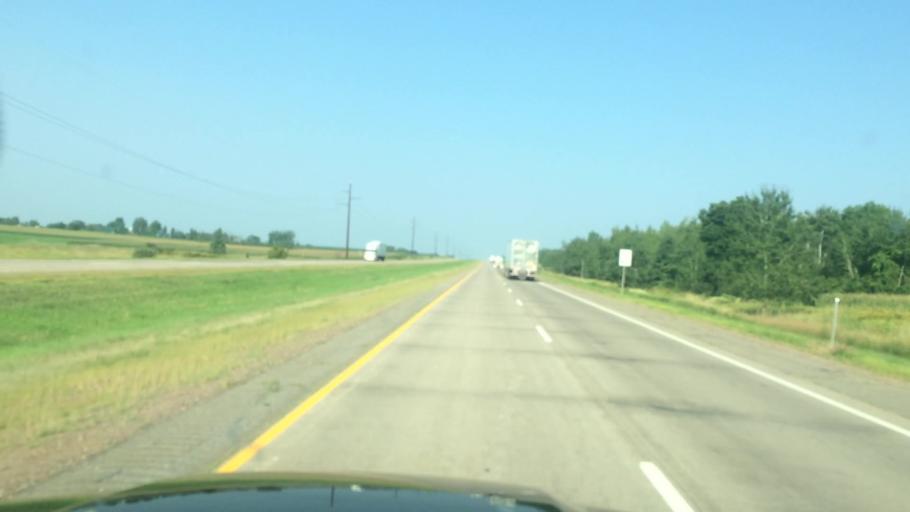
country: US
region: Wisconsin
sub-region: Marathon County
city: Edgar
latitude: 44.9445
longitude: -89.9759
